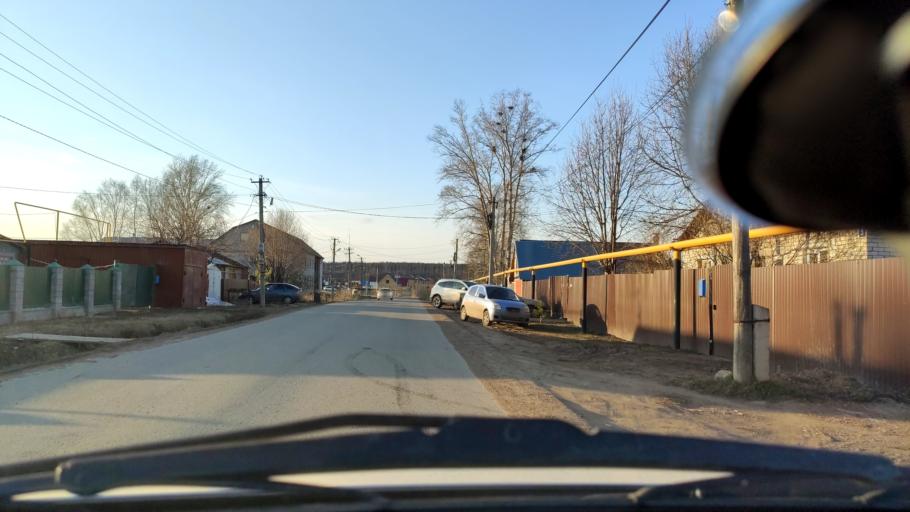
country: RU
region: Bashkortostan
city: Kabakovo
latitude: 54.6543
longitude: 56.1954
